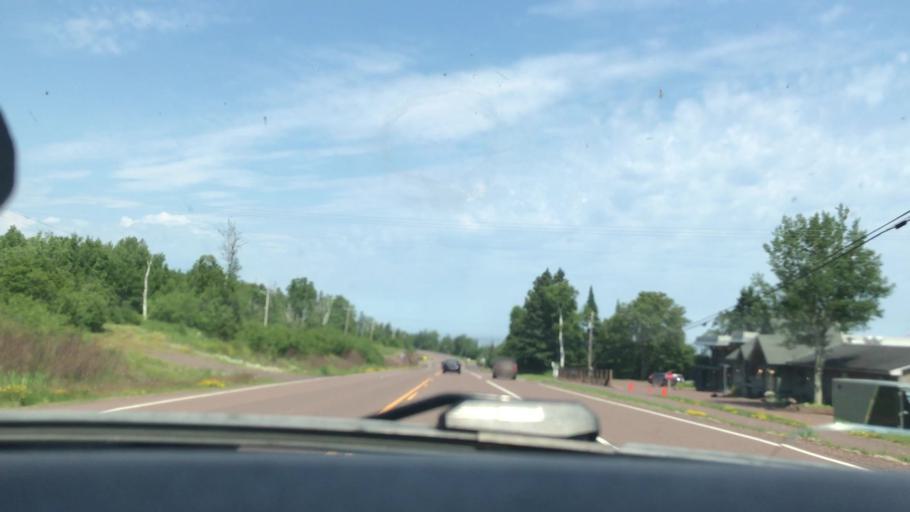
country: US
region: Minnesota
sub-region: Cook County
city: Grand Marais
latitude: 47.6074
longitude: -90.7753
